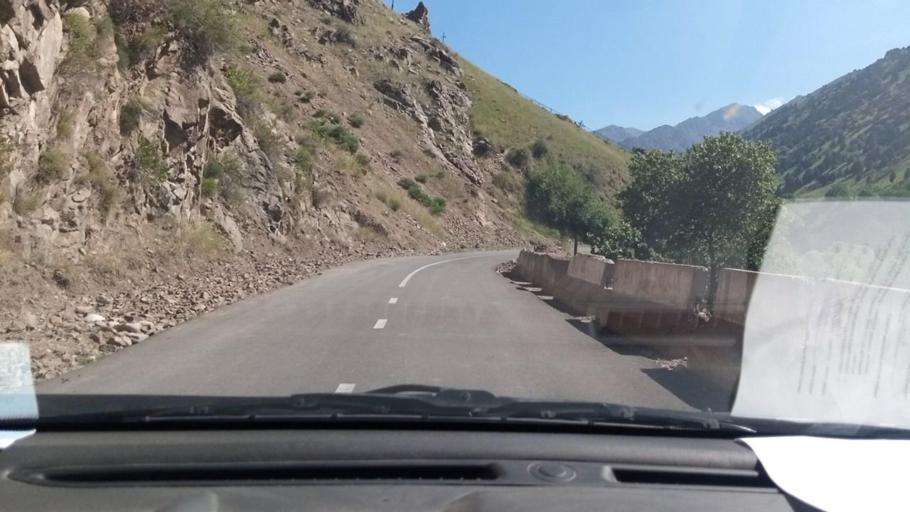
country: UZ
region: Toshkent
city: Yangiobod
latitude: 41.1244
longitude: 70.1053
